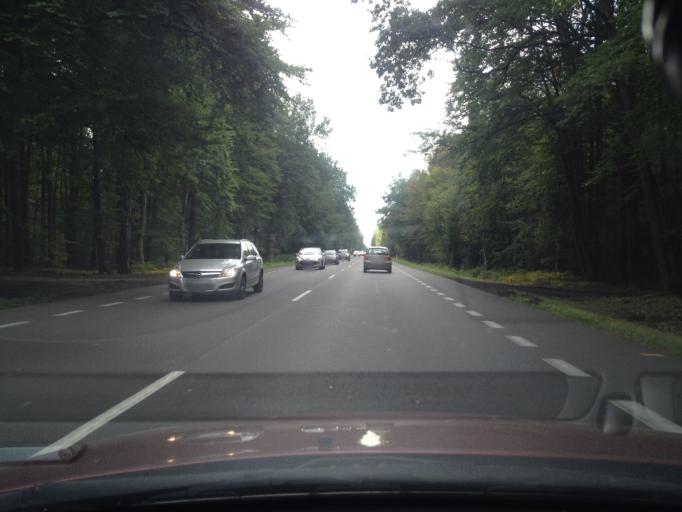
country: PL
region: West Pomeranian Voivodeship
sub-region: Powiat goleniowski
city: Przybiernow
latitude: 53.6706
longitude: 14.8143
